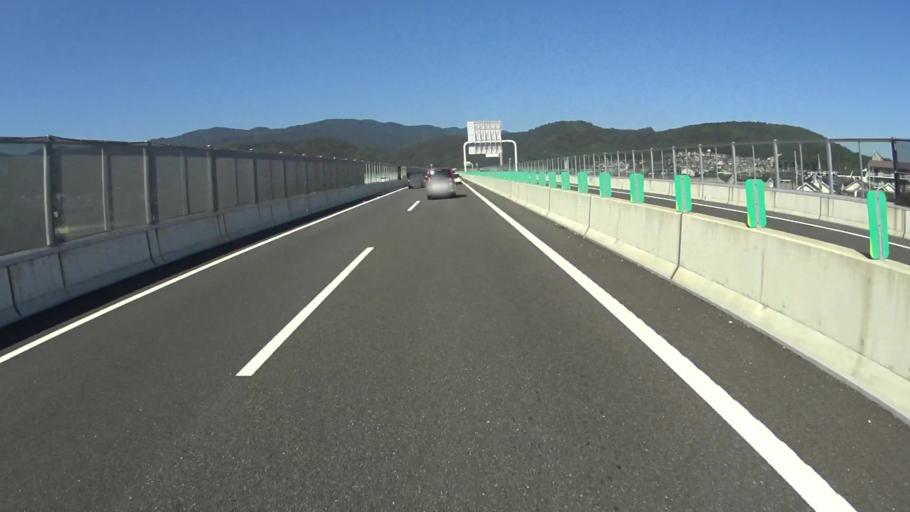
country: JP
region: Kyoto
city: Muko
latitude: 34.9183
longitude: 135.6813
